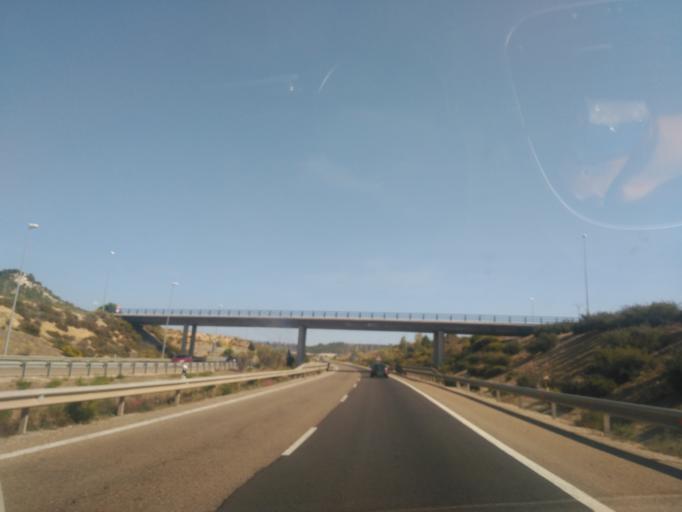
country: ES
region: Castille and Leon
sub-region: Provincia de Valladolid
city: Cisterniga
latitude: 41.6167
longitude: -4.6863
